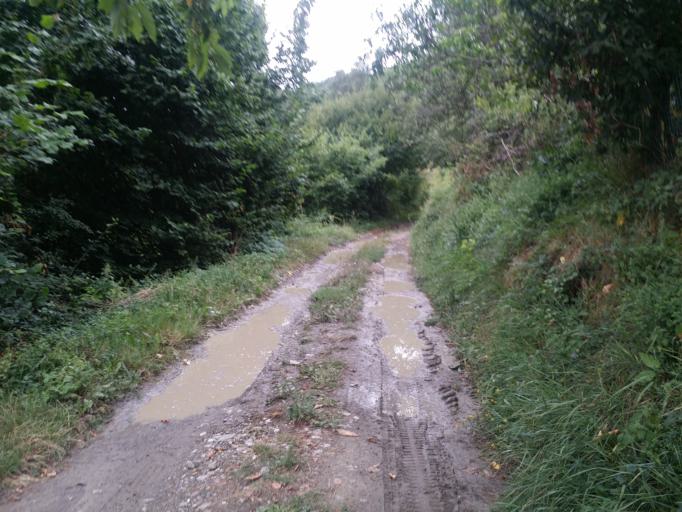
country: IT
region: Emilia-Romagna
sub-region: Provincia di Parma
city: Borgo Val di Taro
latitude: 44.5373
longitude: 9.7853
